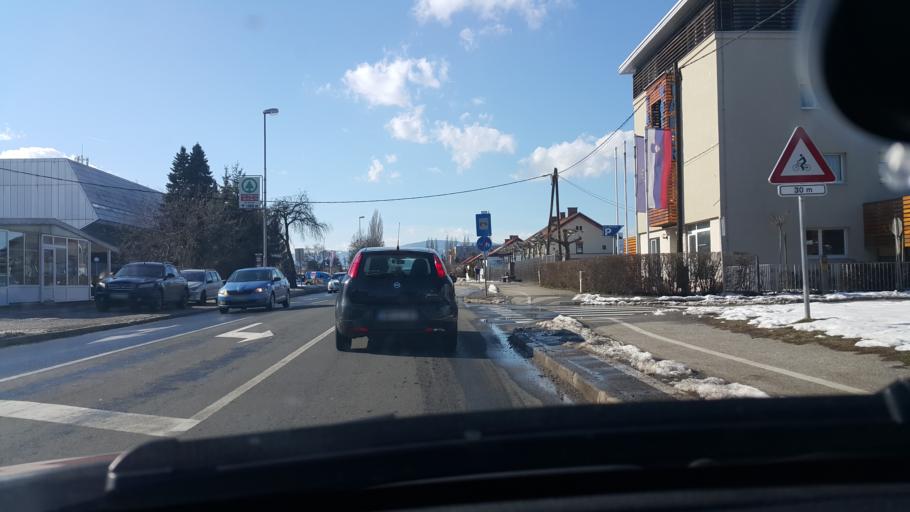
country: SI
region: Maribor
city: Maribor
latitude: 46.5498
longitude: 15.6374
